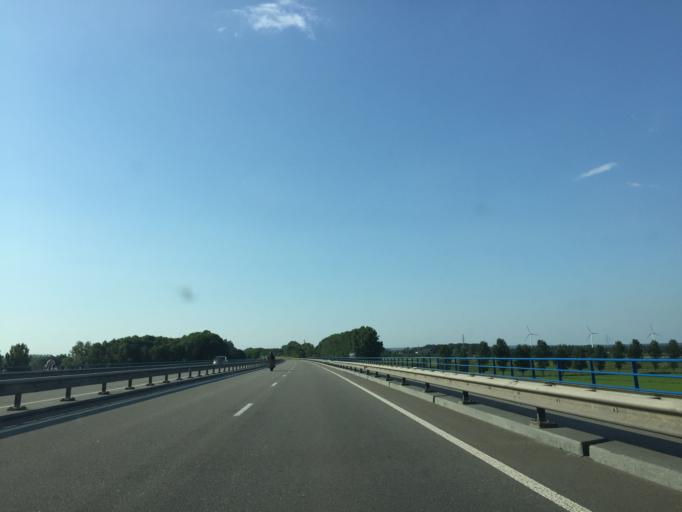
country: NL
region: Gelderland
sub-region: Gemeente Buren
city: Lienden
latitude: 51.8963
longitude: 5.4971
